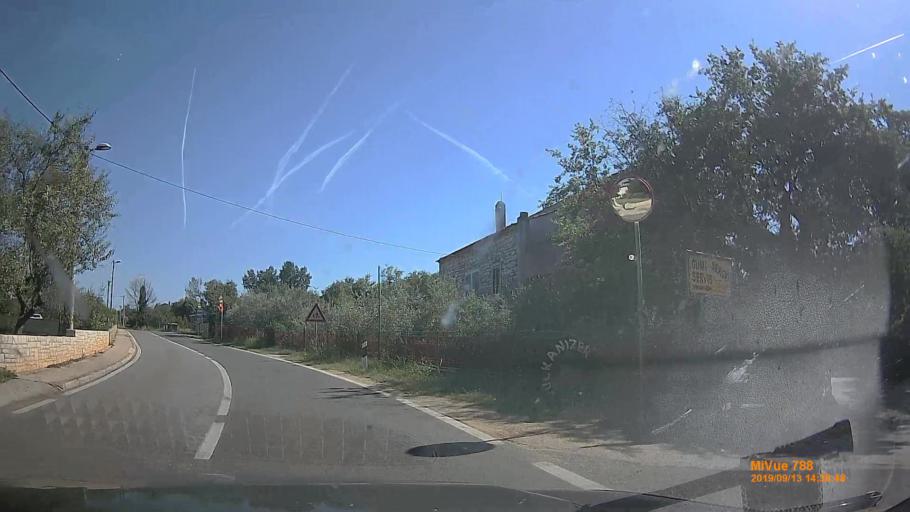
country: HR
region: Istarska
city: Umag
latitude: 45.3990
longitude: 13.5389
